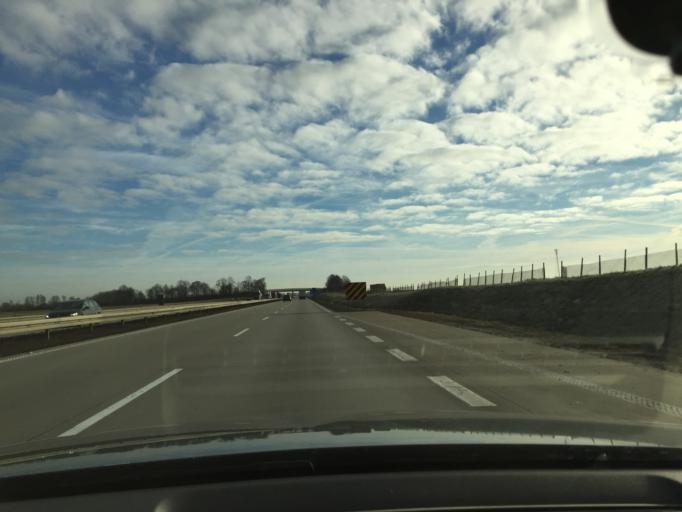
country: PL
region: Lower Silesian Voivodeship
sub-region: Powiat sredzki
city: Udanin
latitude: 51.0588
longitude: 16.5260
